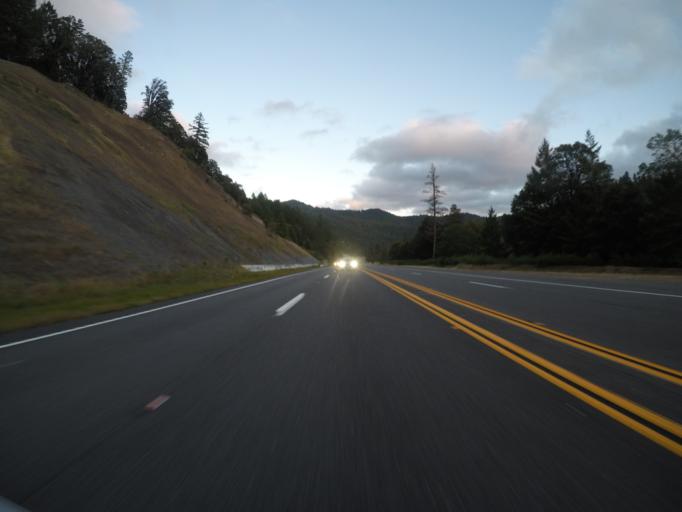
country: US
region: California
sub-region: Humboldt County
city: Redway
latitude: 40.0437
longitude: -123.7812
